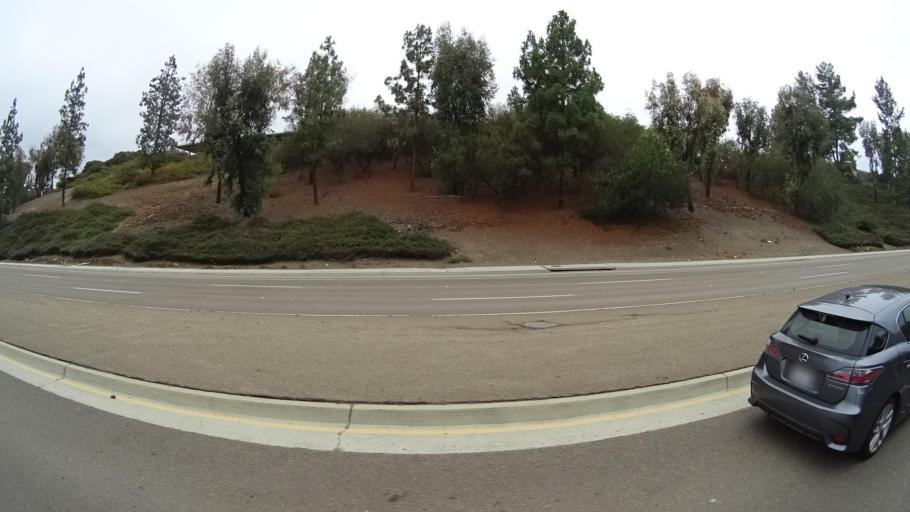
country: US
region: California
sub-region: San Diego County
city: Poway
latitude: 32.9929
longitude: -117.0752
